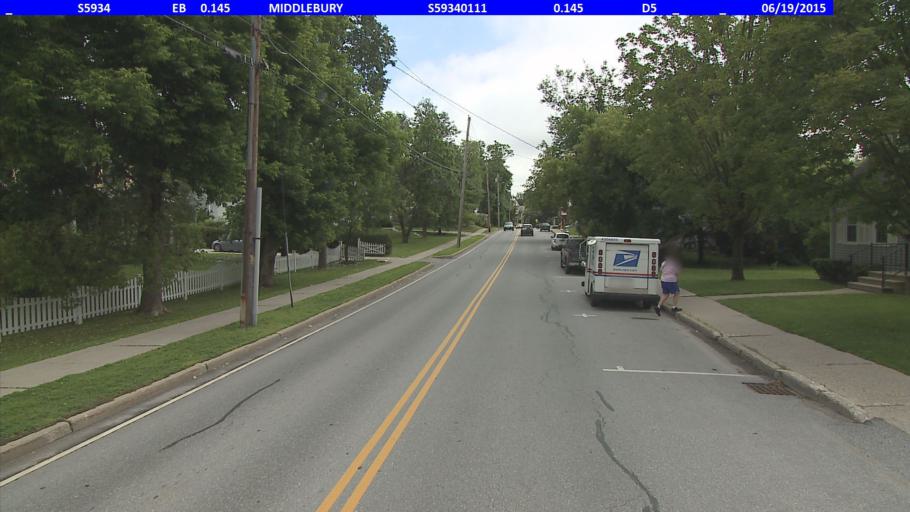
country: US
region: Vermont
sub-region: Addison County
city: Middlebury (village)
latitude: 44.0155
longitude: -73.1634
